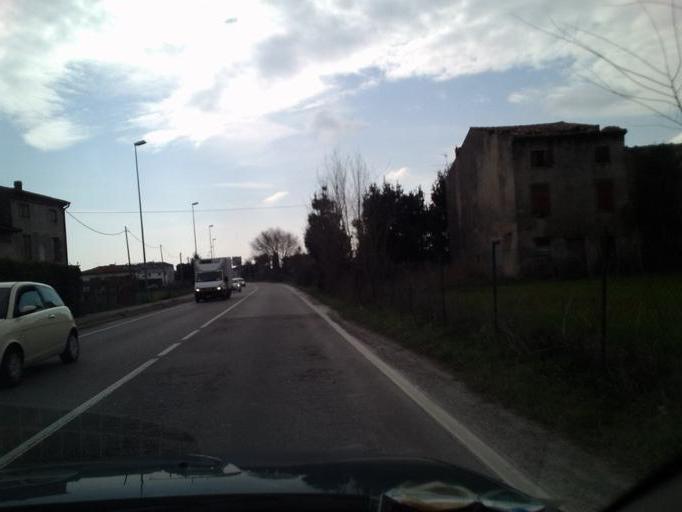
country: IT
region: Veneto
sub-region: Provincia di Verona
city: Villafranca di Verona
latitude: 45.3642
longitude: 10.8457
